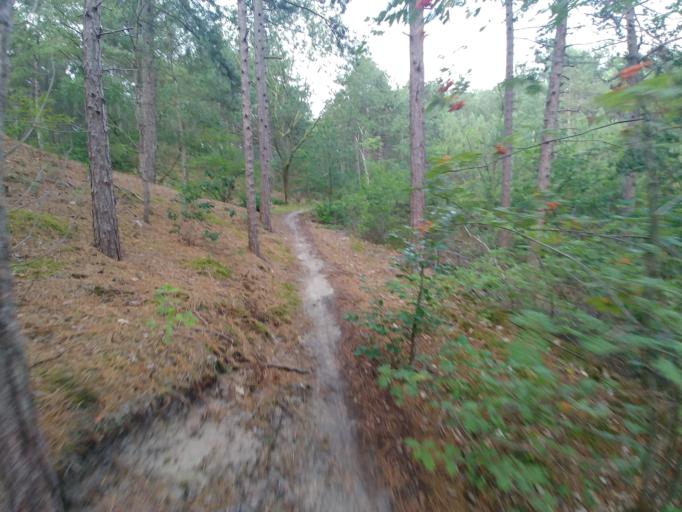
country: NL
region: North Holland
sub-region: Gemeente Alkmaar
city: Alkmaar
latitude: 52.6865
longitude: 4.6900
